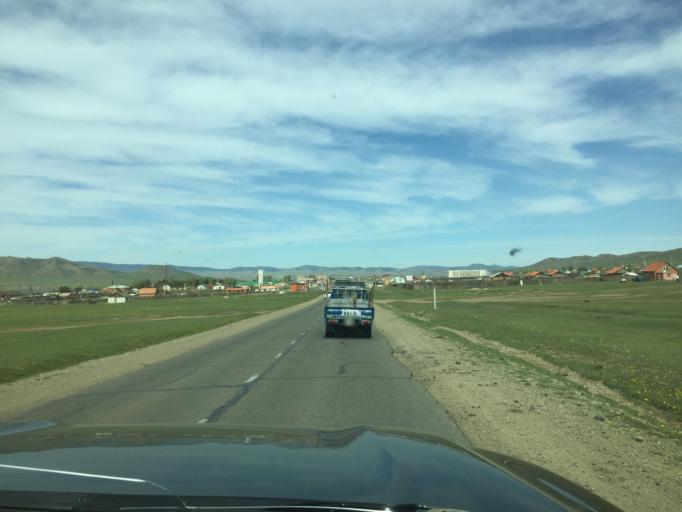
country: MN
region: Central Aimak
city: Ihsueuej
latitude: 48.2190
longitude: 106.3026
